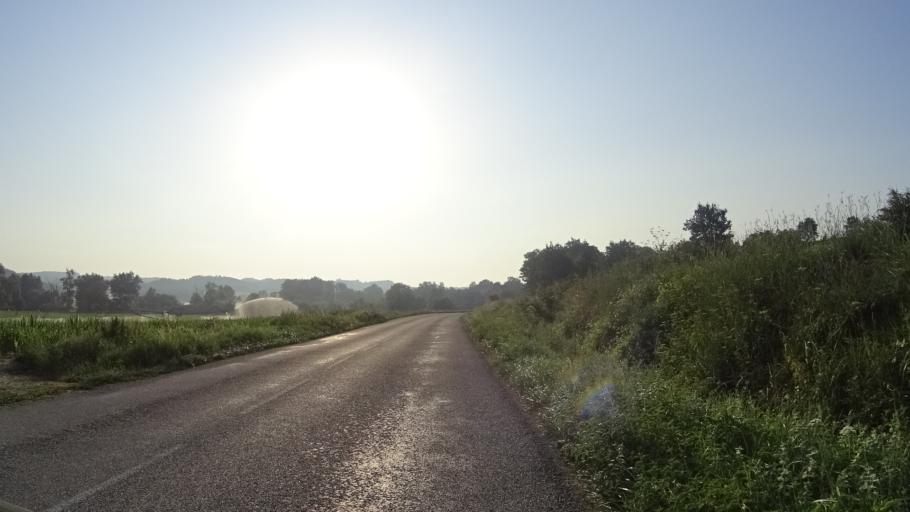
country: FR
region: Midi-Pyrenees
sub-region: Departement de l'Ariege
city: Mirepoix
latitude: 43.0857
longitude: 1.9206
